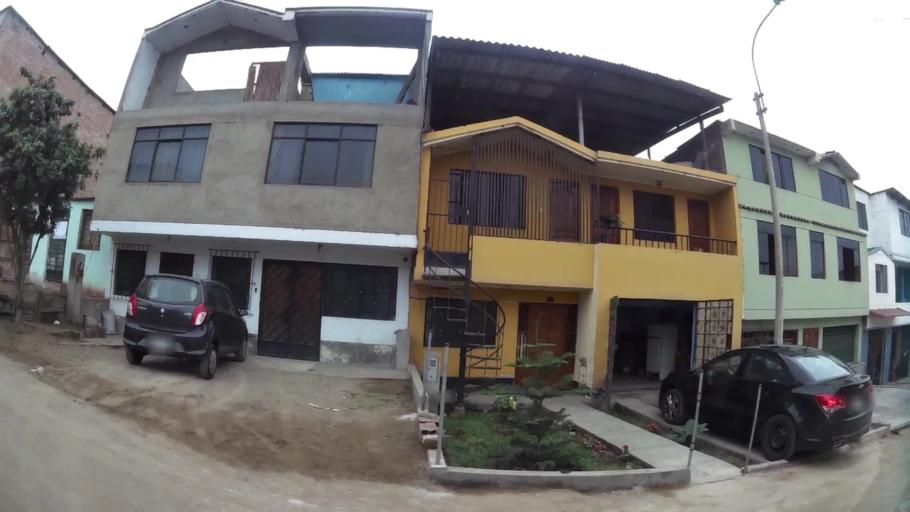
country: PE
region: Lima
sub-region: Lima
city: Surco
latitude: -12.1742
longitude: -76.9578
